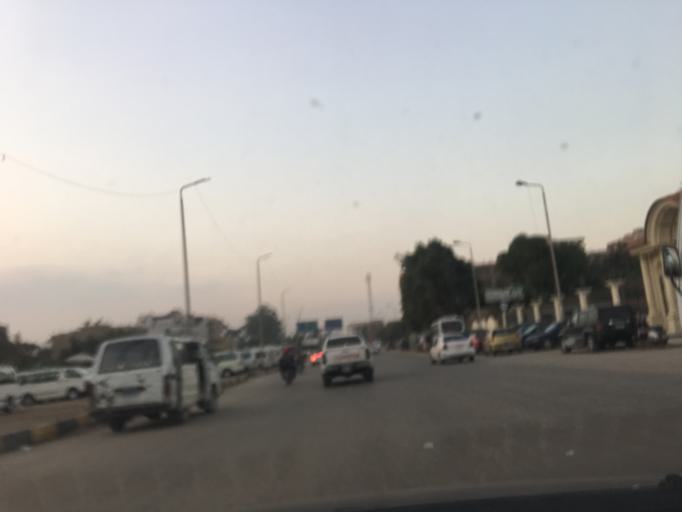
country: EG
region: Al Jizah
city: Al Jizah
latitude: 29.9914
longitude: 31.1308
